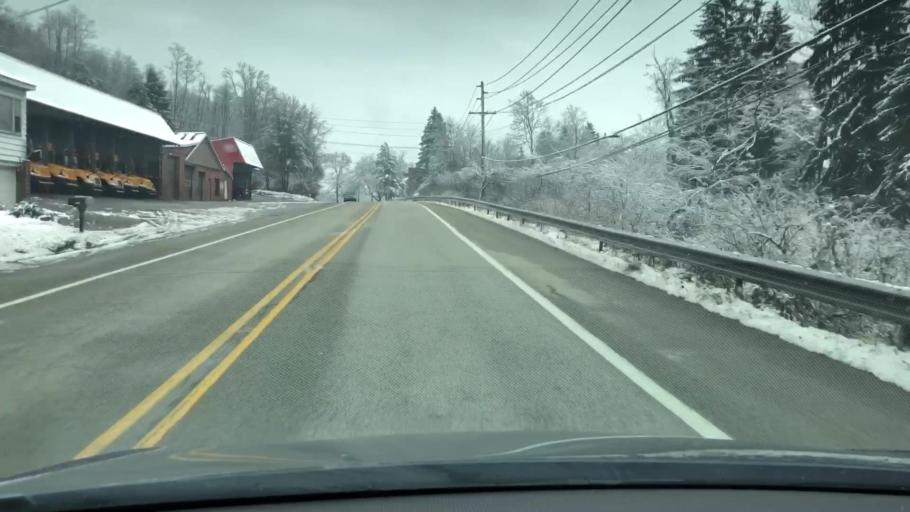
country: US
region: Pennsylvania
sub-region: Fayette County
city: Hopwood
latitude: 39.8197
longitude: -79.5892
